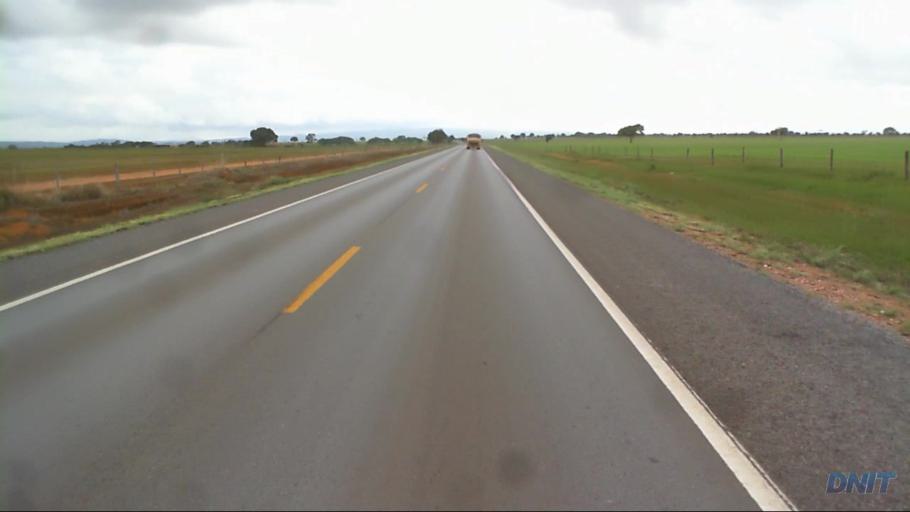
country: BR
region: Goias
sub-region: Padre Bernardo
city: Padre Bernardo
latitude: -15.2192
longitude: -48.6305
